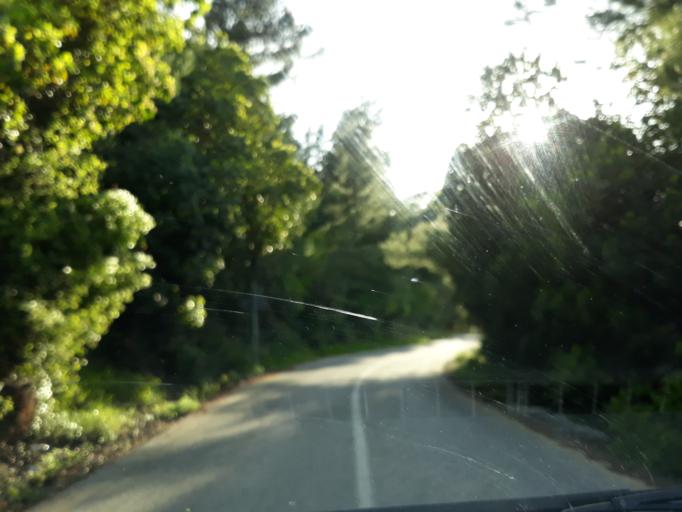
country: GR
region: Attica
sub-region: Nomarchia Anatolikis Attikis
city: Afidnes
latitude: 38.2251
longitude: 23.7899
